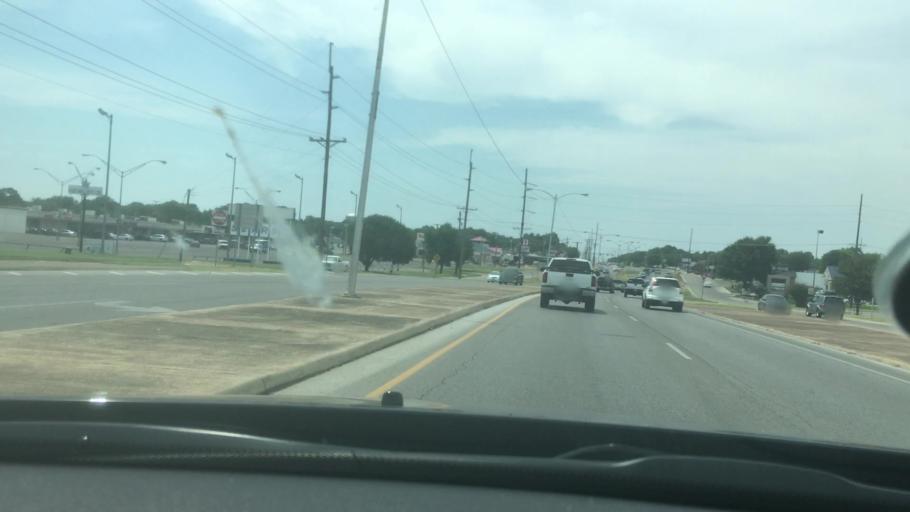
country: US
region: Oklahoma
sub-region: Carter County
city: Ardmore
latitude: 34.1800
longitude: -97.1431
